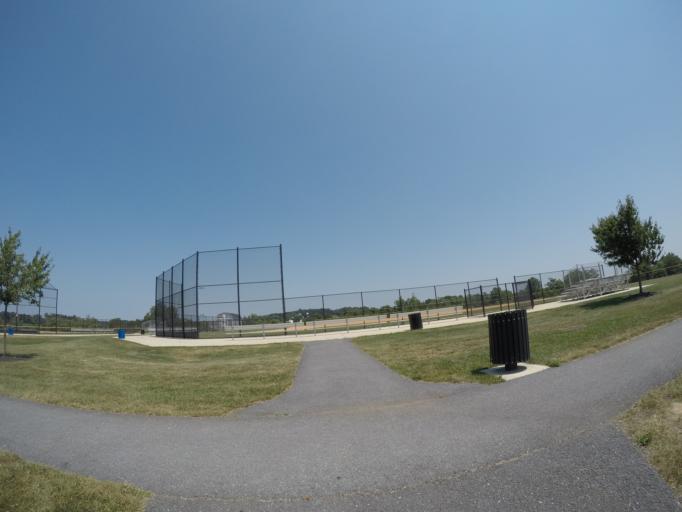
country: US
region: Maryland
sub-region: Frederick County
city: Urbana
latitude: 39.3380
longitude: -77.3649
